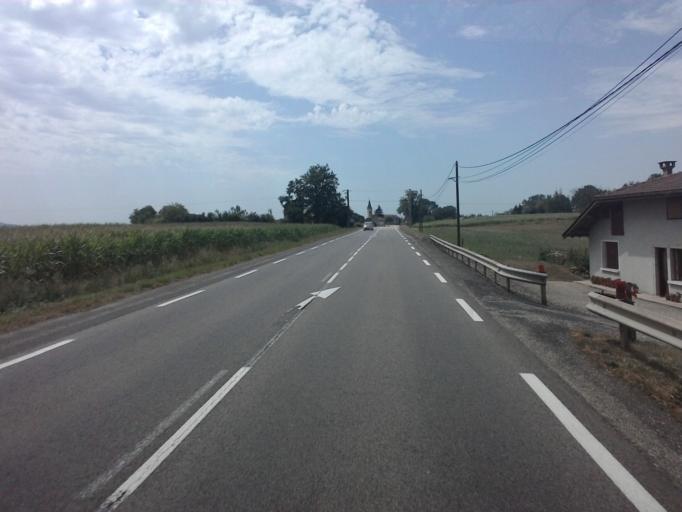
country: FR
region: Rhone-Alpes
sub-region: Departement de l'Ain
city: Coligny
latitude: 46.3509
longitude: 5.3247
